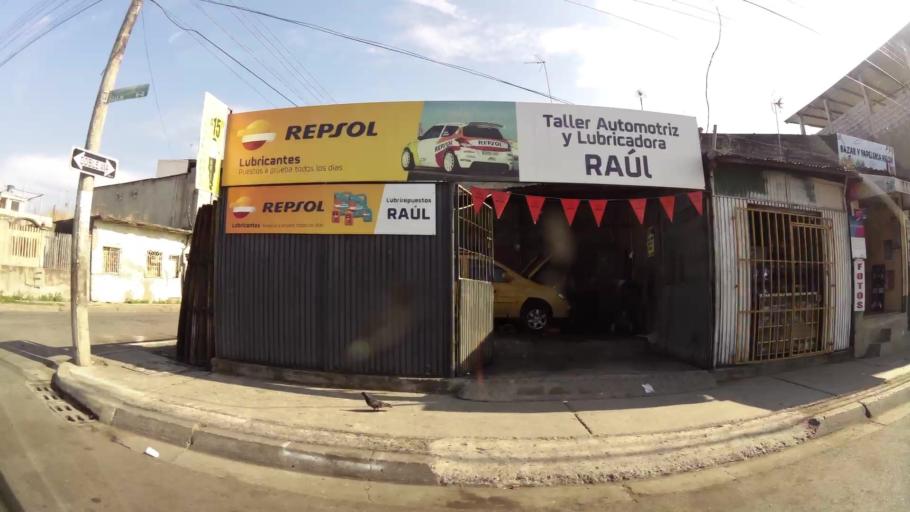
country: EC
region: Guayas
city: Eloy Alfaro
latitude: -2.0933
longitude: -79.9163
